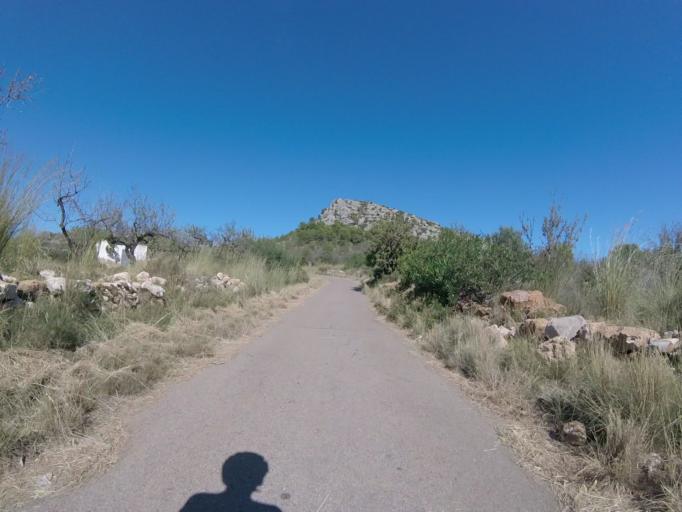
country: ES
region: Valencia
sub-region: Provincia de Castello
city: Orpesa/Oropesa del Mar
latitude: 40.1360
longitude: 0.1050
